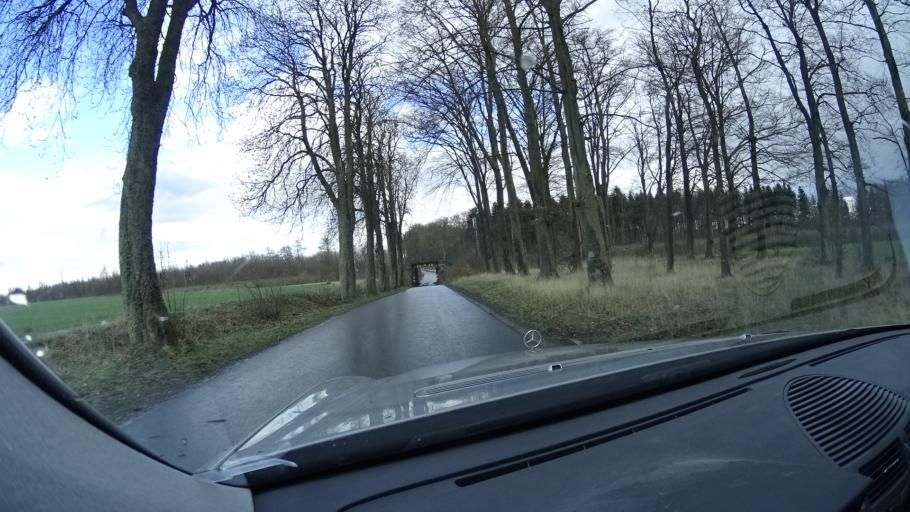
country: SE
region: Skane
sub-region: Eslovs Kommun
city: Eslov
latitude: 55.8155
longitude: 13.2942
